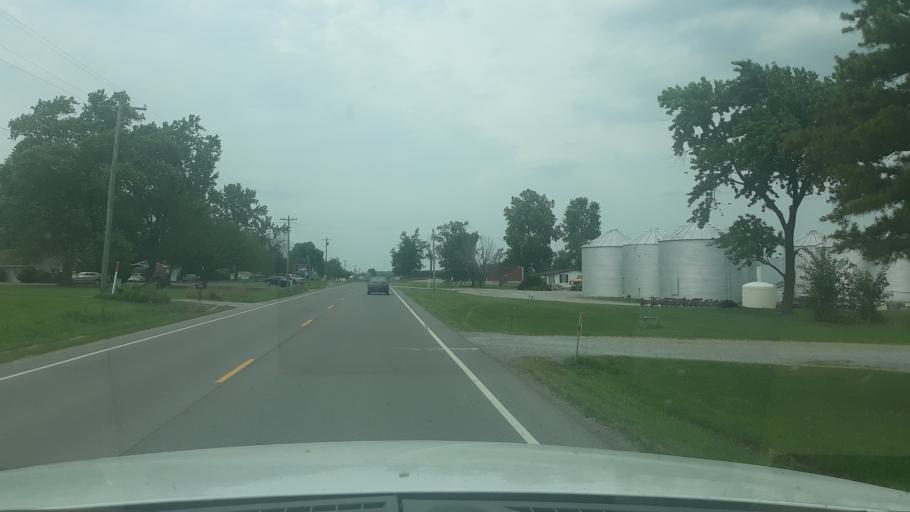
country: US
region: Illinois
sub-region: Saline County
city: Harrisburg
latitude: 37.7975
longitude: -88.5399
